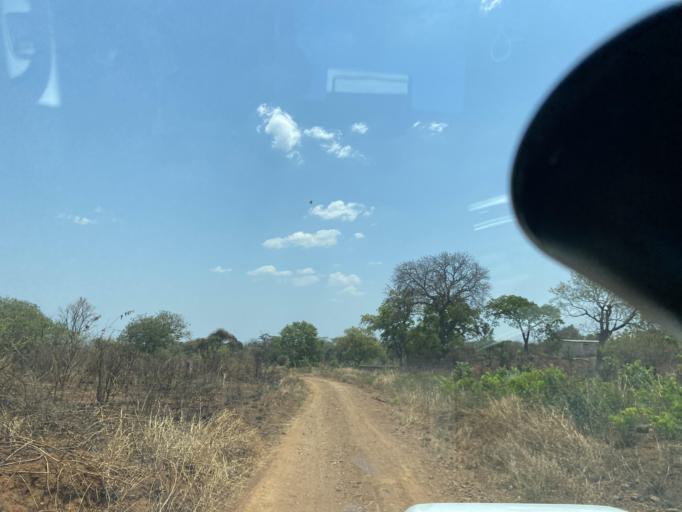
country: ZM
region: Lusaka
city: Lusaka
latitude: -15.5051
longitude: 28.0106
